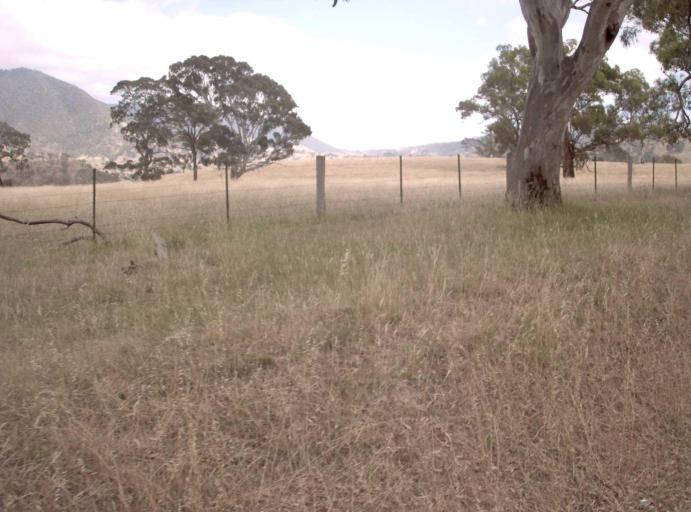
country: AU
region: Victoria
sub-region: Wellington
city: Heyfield
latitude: -37.6530
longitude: 146.6425
